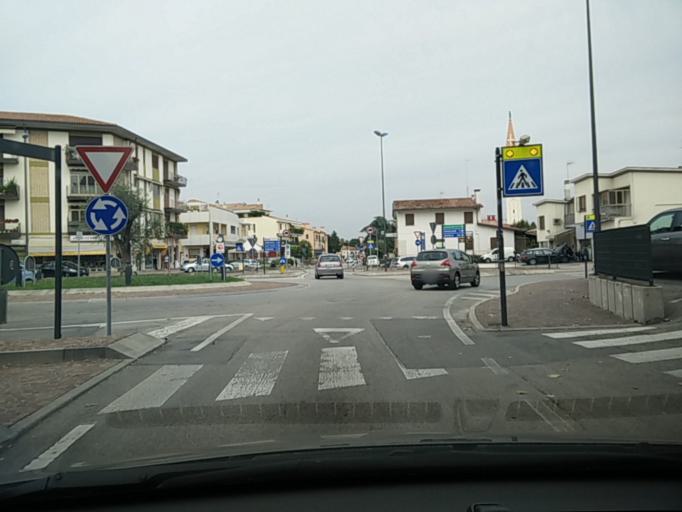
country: IT
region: Veneto
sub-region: Provincia di Treviso
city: Silea
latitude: 45.6533
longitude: 12.2956
